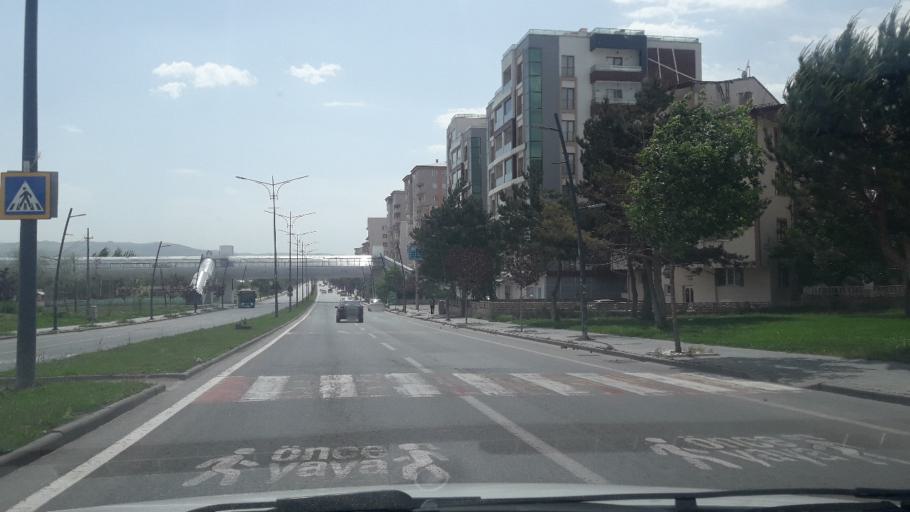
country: TR
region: Sivas
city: Sivas
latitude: 39.7317
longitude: 36.9846
